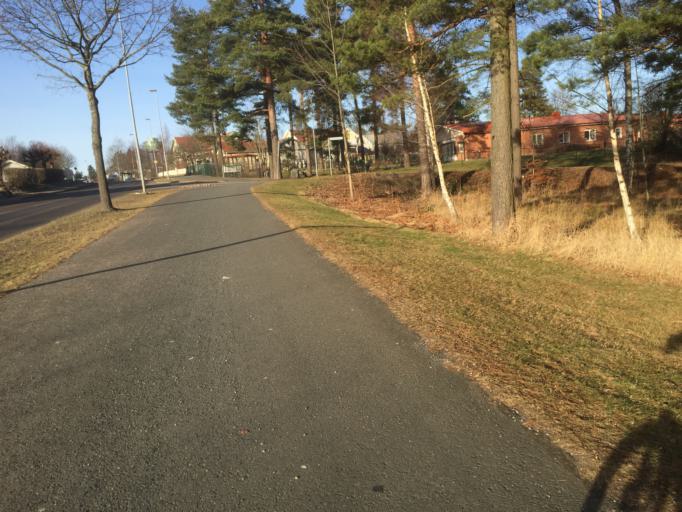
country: SE
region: Joenkoeping
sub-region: Aneby Kommun
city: Aneby
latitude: 57.8391
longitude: 14.8075
